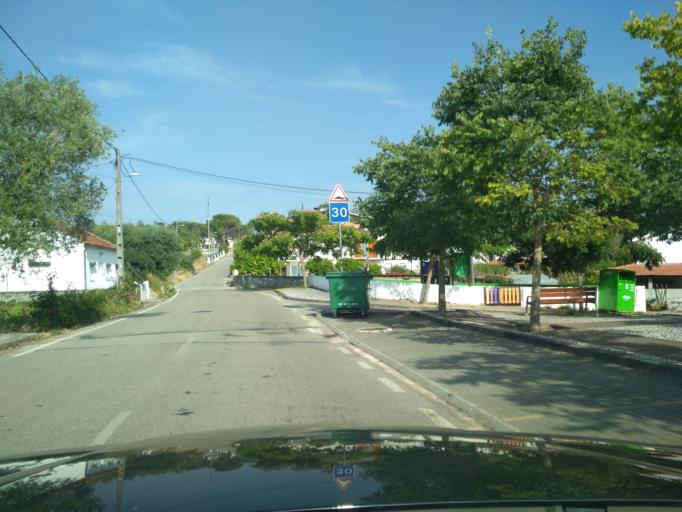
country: PT
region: Coimbra
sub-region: Condeixa-A-Nova
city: Condeixa-a-Nova
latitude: 40.1308
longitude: -8.4628
